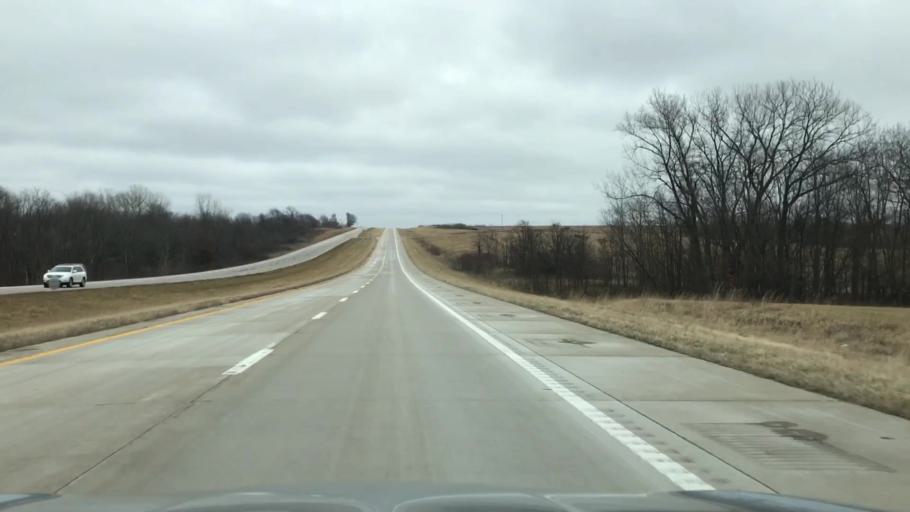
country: US
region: Missouri
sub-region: Livingston County
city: Chillicothe
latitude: 39.7379
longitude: -93.6997
